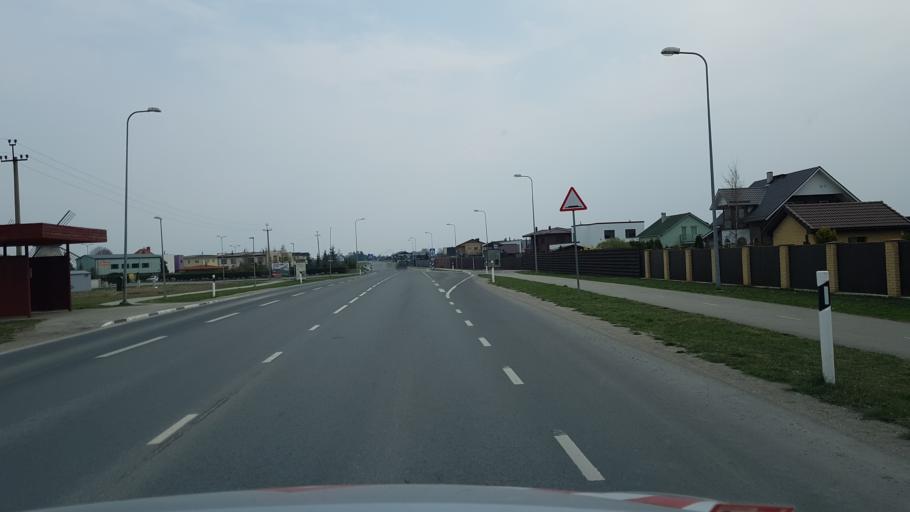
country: EE
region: Harju
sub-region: Tallinna linn
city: Tallinn
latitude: 59.3903
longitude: 24.8027
